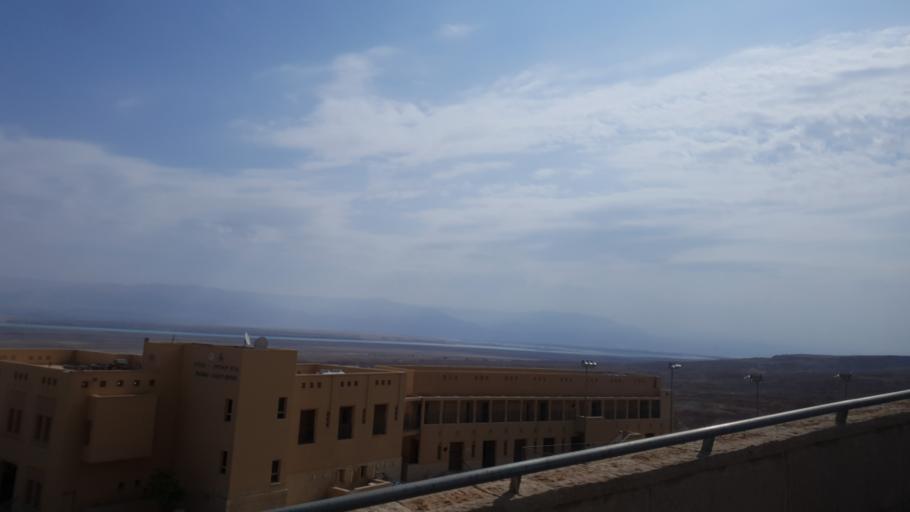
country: IL
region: Southern District
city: `En Boqeq
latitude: 31.3105
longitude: 35.3634
